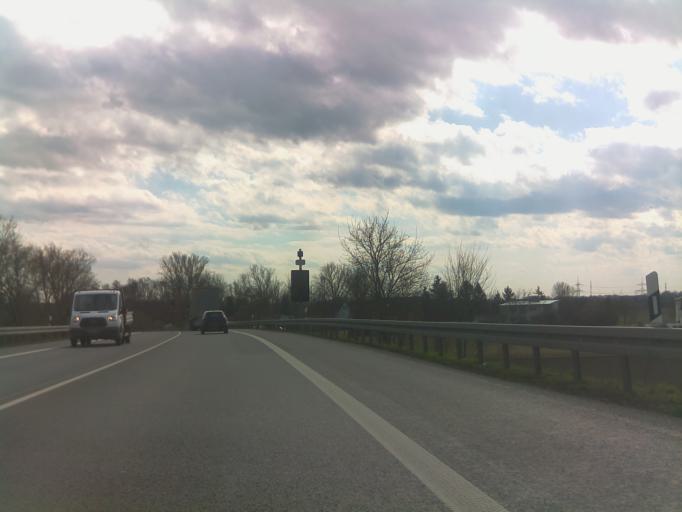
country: DE
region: Hesse
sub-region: Regierungsbezirk Darmstadt
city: Burstadt
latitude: 49.6466
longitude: 8.4466
